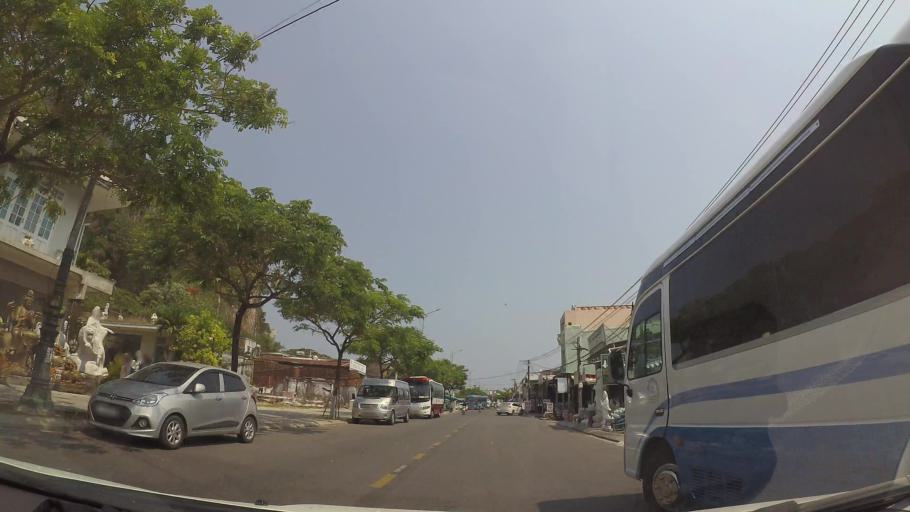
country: VN
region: Da Nang
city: Ngu Hanh Son
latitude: 16.0025
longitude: 108.2616
